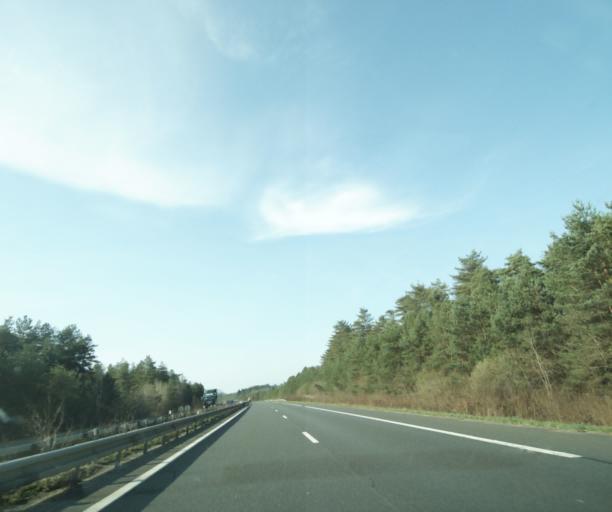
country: FR
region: Centre
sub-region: Departement du Loir-et-Cher
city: Lamotte-Beuvron
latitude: 47.5915
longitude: 1.9874
